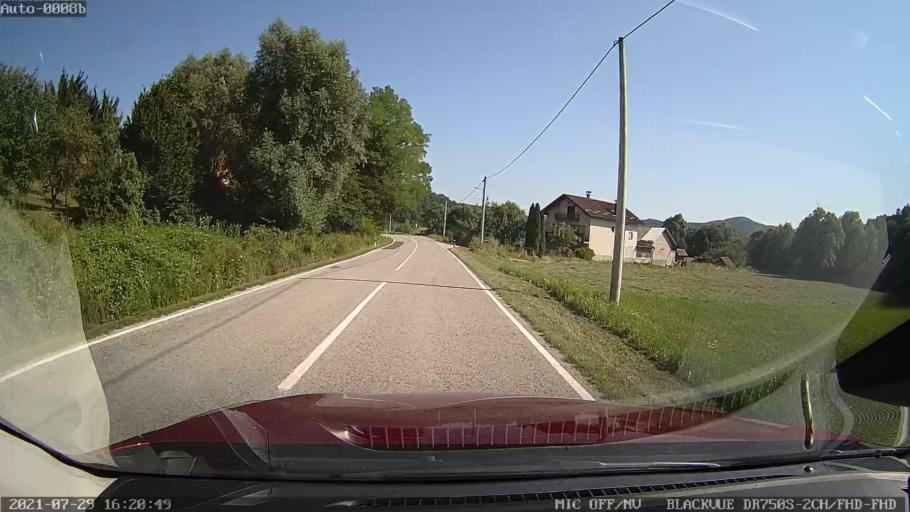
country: HR
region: Varazdinska
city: Lepoglava
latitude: 46.2379
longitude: 15.9636
